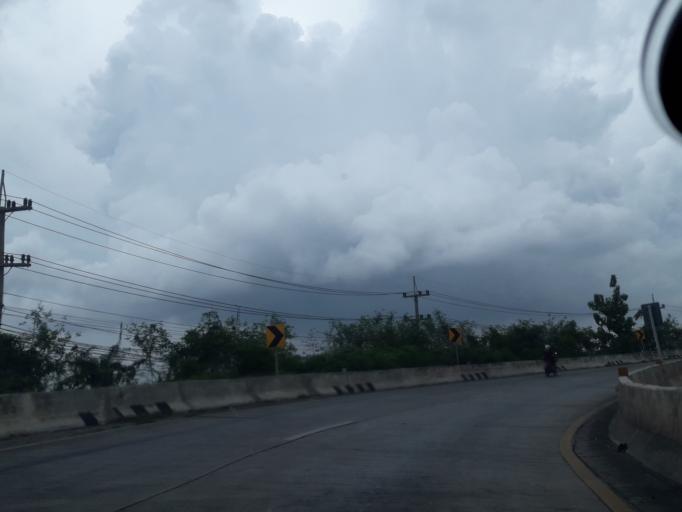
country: TH
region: Sara Buri
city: Kaeng Khoi
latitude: 14.5814
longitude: 101.0018
